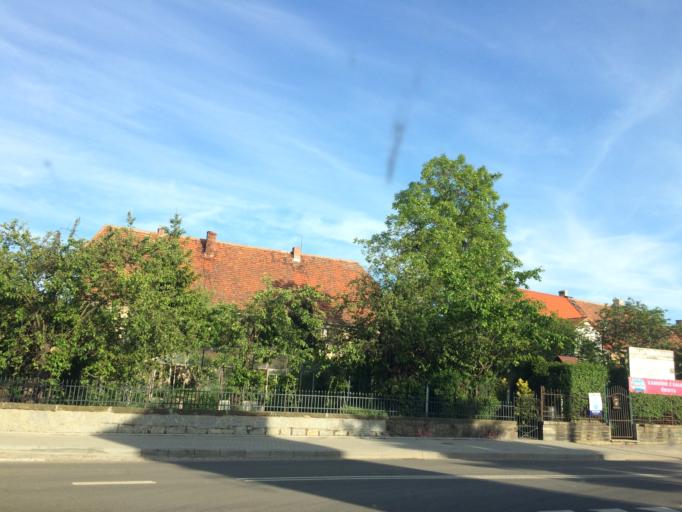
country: PL
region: Lower Silesian Voivodeship
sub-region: Powiat swidnicki
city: Swidnica
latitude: 50.8263
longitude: 16.4891
